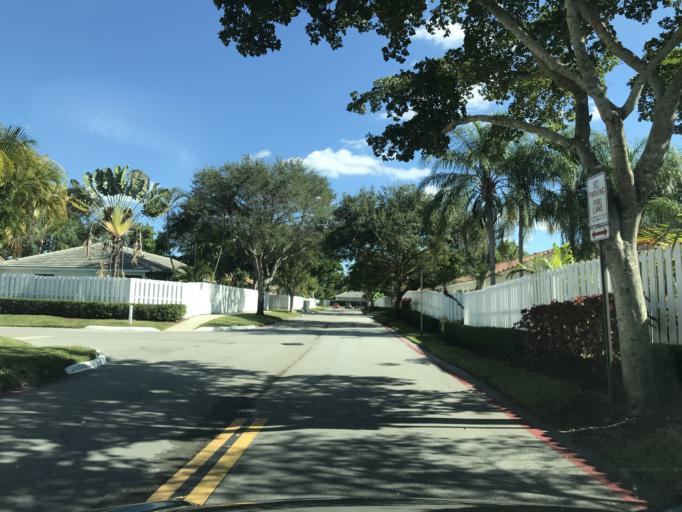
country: US
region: Florida
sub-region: Broward County
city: Pine Island Ridge
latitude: 26.1345
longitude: -80.2777
